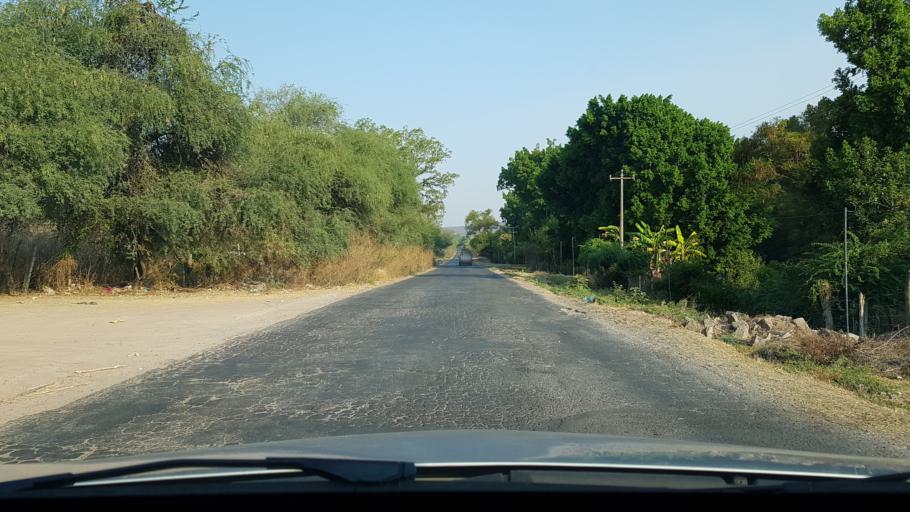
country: MX
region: Morelos
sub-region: Tepalcingo
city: Zacapalco
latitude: 18.6443
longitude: -99.0217
